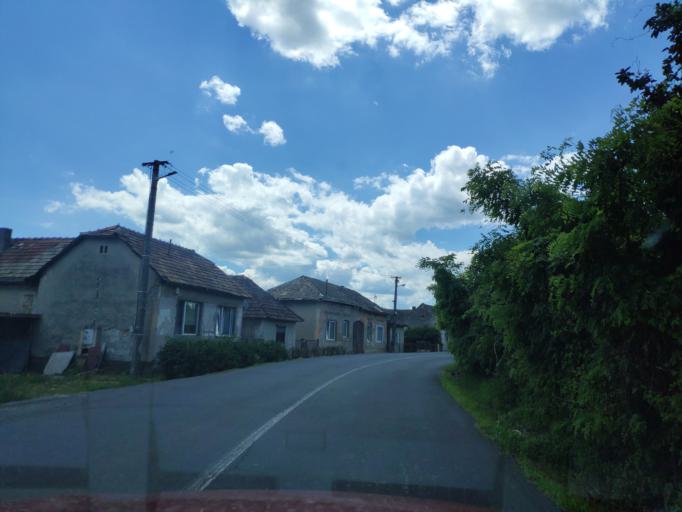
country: HU
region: Borsod-Abauj-Zemplen
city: Ozd
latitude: 48.3045
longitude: 20.2458
